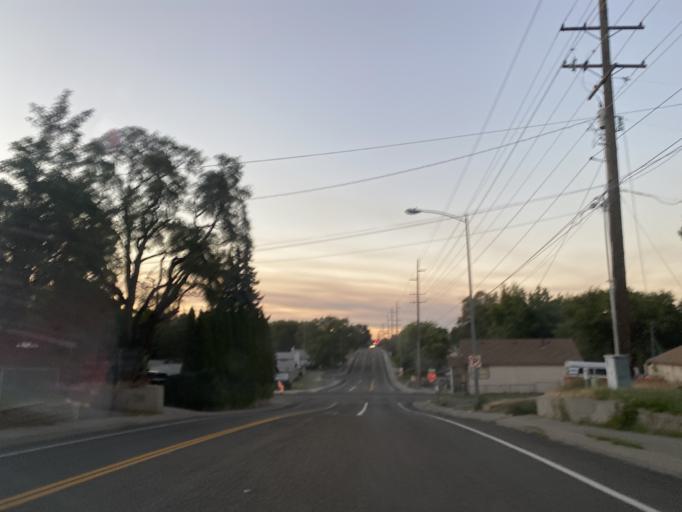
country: US
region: Washington
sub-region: Benton County
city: Kennewick
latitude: 46.2020
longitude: -119.1696
